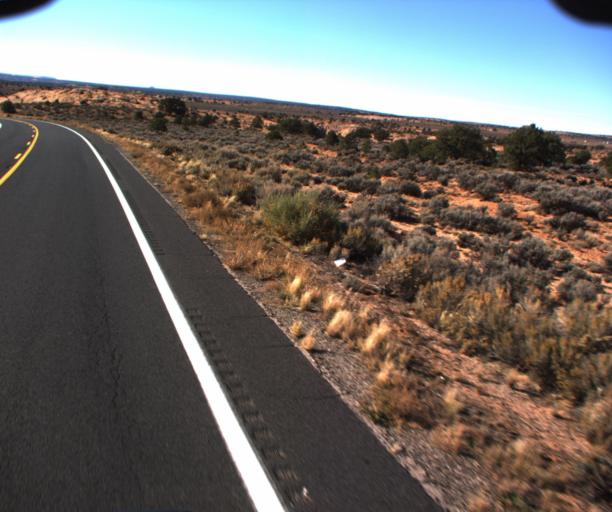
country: US
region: Arizona
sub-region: Coconino County
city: Kaibito
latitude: 36.5634
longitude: -110.7351
